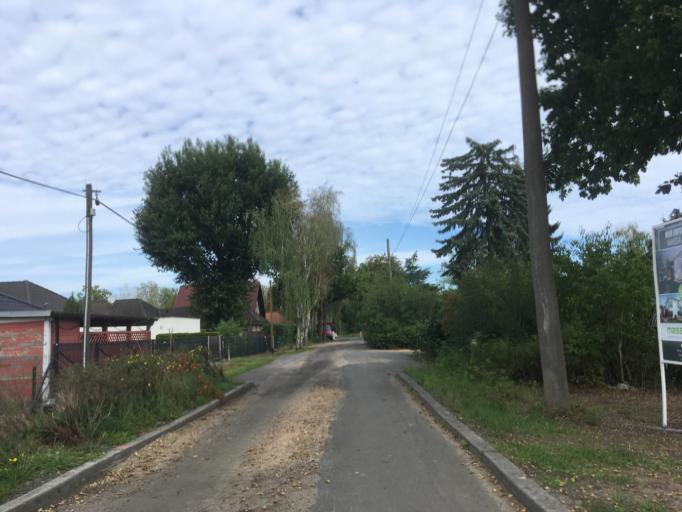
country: DE
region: Brandenburg
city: Wandlitz
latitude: 52.7539
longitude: 13.3927
